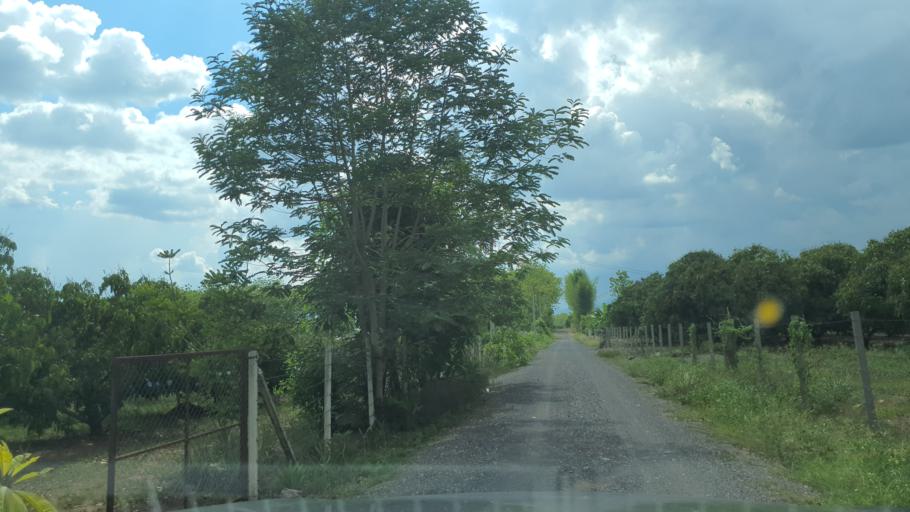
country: TH
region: Chiang Mai
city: Mae Taeng
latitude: 19.1237
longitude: 99.0506
